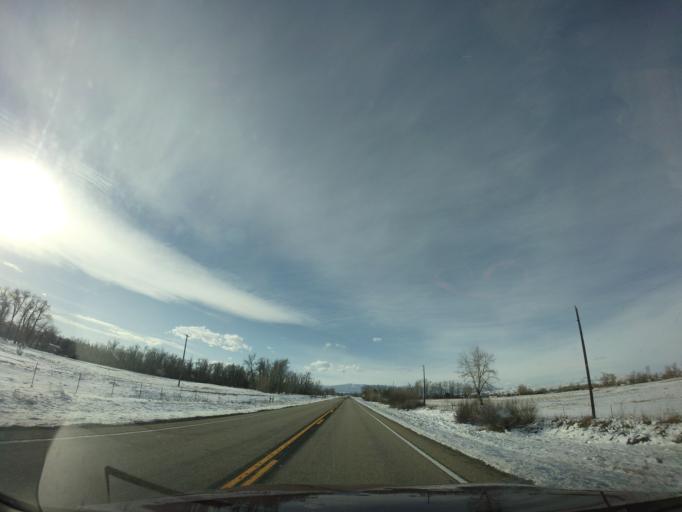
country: US
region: Montana
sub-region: Carbon County
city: Red Lodge
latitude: 45.3786
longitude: -109.1498
